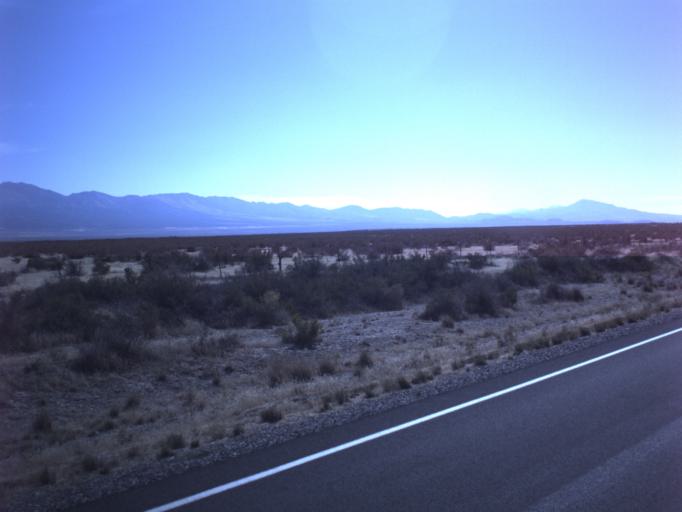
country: US
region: Utah
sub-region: Tooele County
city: Grantsville
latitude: 40.3327
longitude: -112.7445
